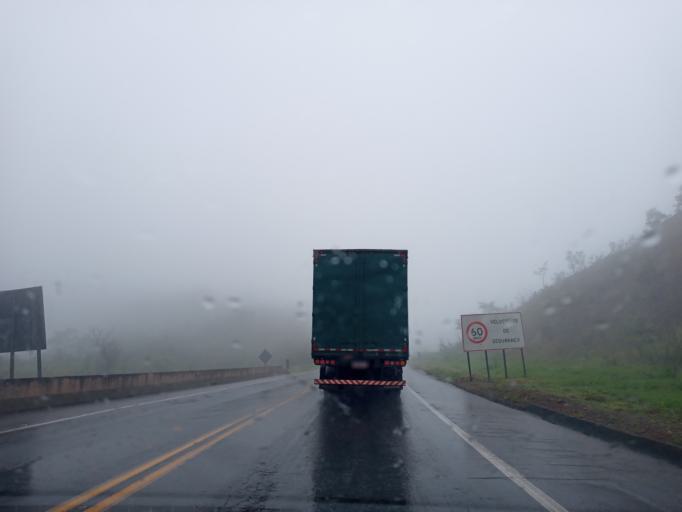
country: BR
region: Minas Gerais
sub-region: Luz
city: Luz
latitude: -19.7094
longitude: -45.9158
